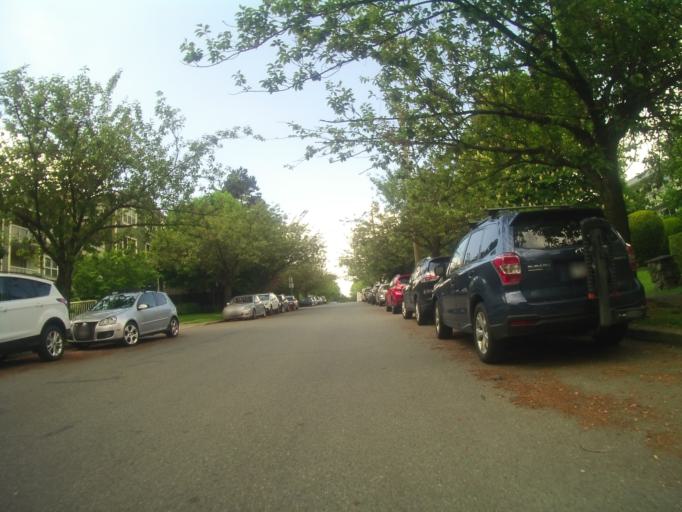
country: CA
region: British Columbia
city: Vancouver
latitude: 49.2652
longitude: -123.0875
